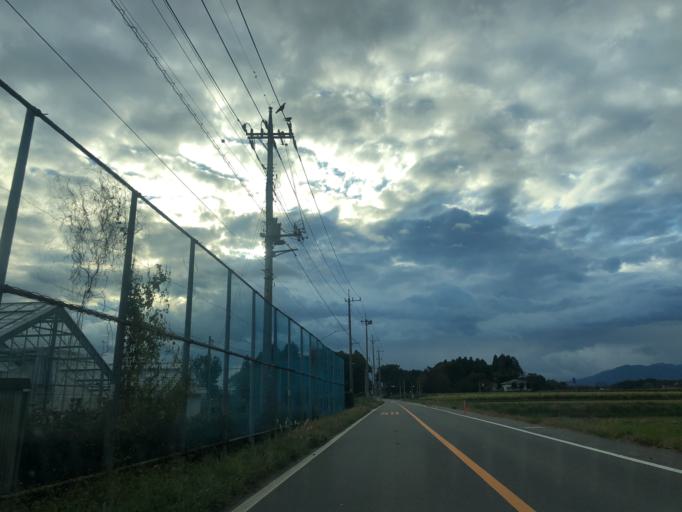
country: JP
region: Tochigi
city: Kuroiso
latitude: 36.9442
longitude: 140.0765
